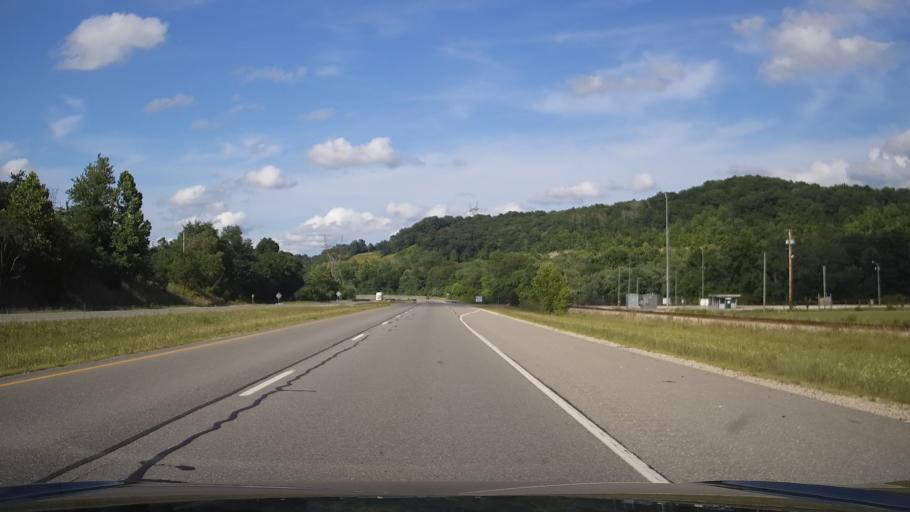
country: US
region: Kentucky
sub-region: Lawrence County
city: Louisa
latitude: 38.1761
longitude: -82.6147
